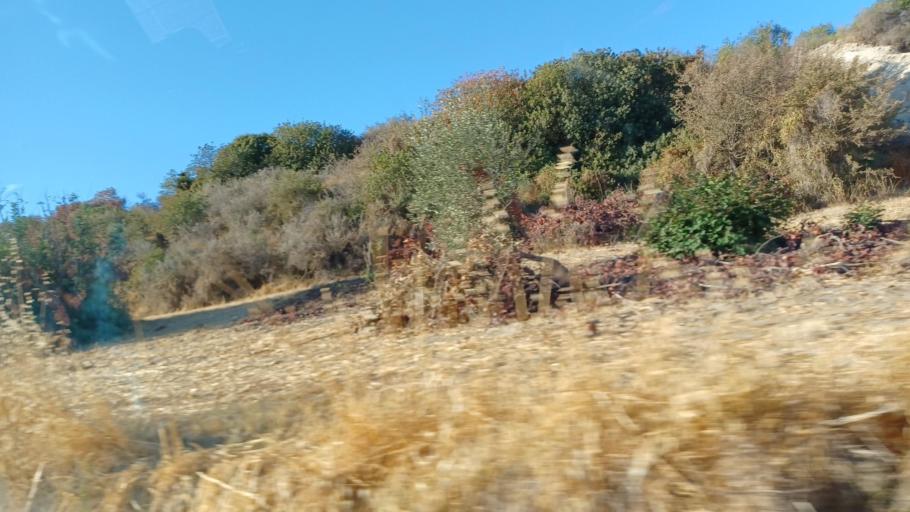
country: CY
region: Pafos
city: Polis
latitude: 34.9760
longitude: 32.4576
